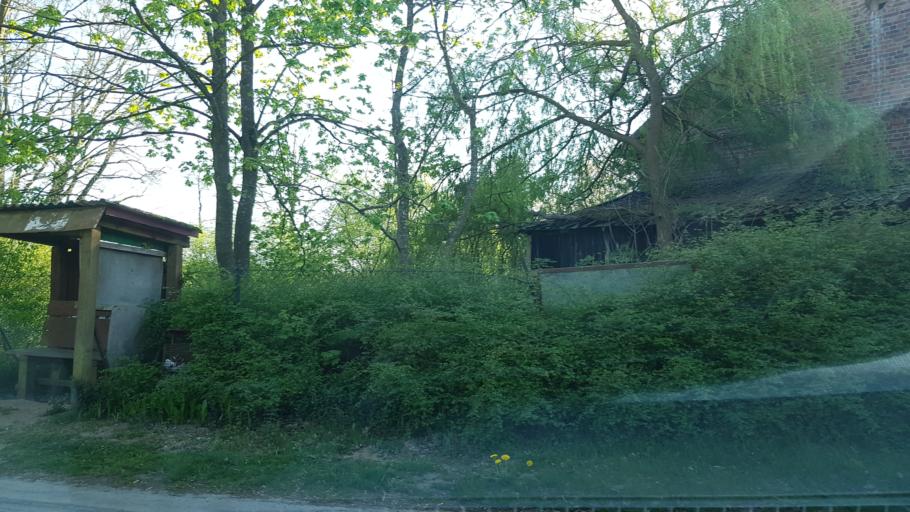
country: DE
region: Lower Saxony
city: Altenmedingen
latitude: 53.1733
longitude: 10.6116
